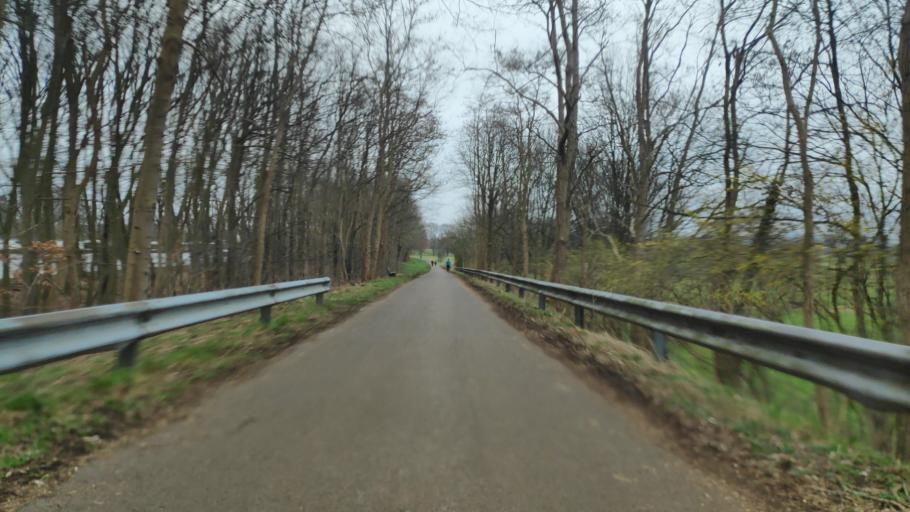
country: DE
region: North Rhine-Westphalia
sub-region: Regierungsbezirk Detmold
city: Minden
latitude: 52.2982
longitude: 8.8527
